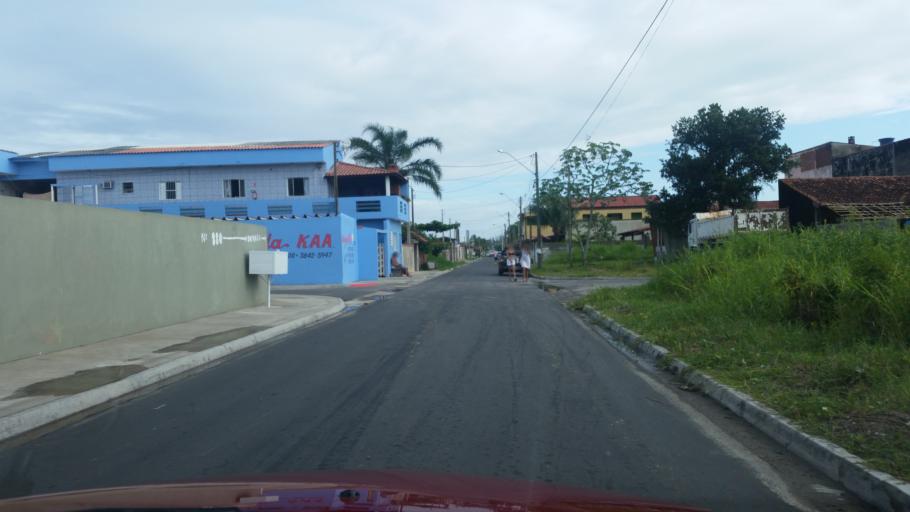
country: BR
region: Sao Paulo
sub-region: Iguape
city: Iguape
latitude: -24.7400
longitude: -47.5513
